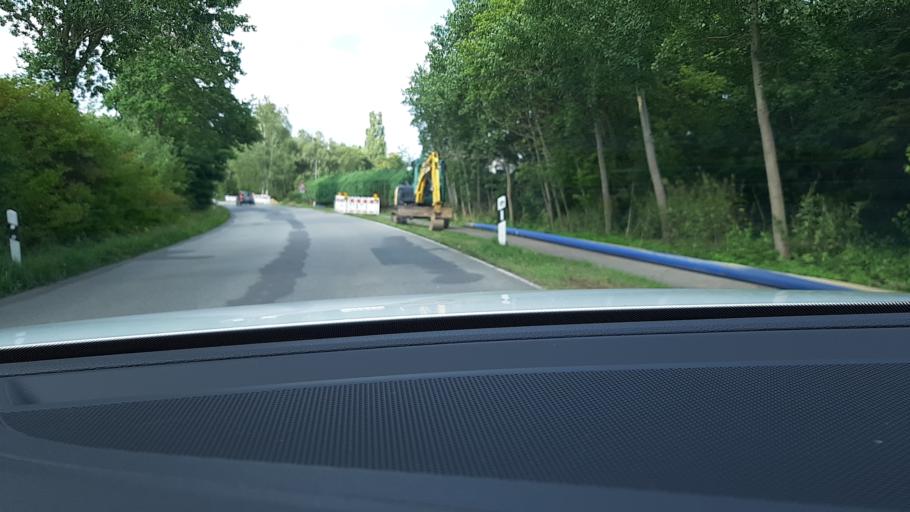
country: DE
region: Schleswig-Holstein
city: Heidekamp
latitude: 53.8414
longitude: 10.4991
